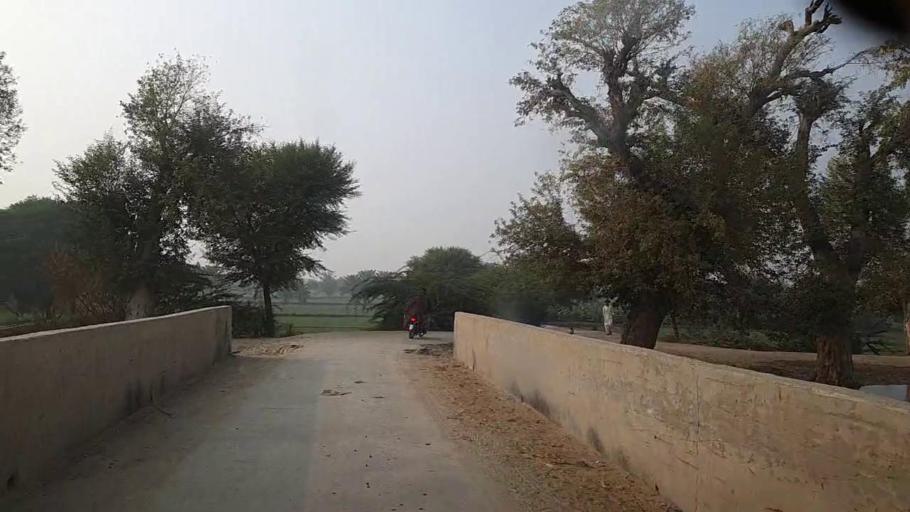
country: PK
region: Sindh
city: Bozdar
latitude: 27.1664
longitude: 68.6625
